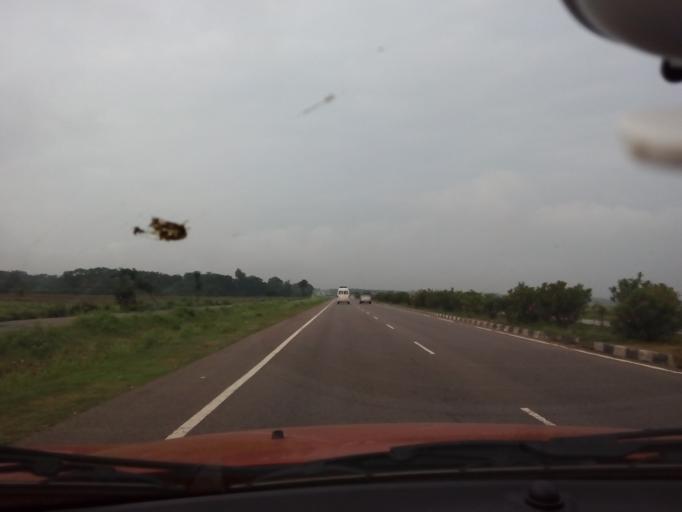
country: IN
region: Karnataka
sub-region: Tumkur
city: Kunigal
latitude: 13.0110
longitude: 77.0366
